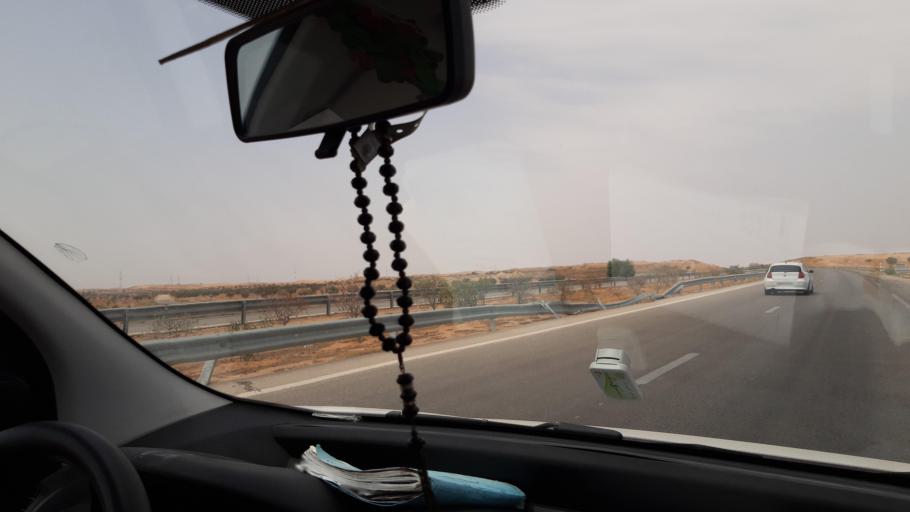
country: TN
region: Safaqis
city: Sfax
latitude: 34.7522
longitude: 10.6049
